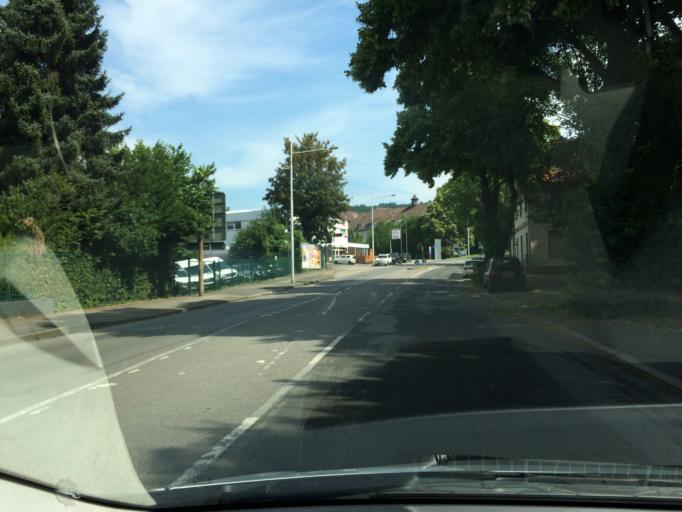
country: DE
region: North Rhine-Westphalia
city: Iserlohn
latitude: 51.3825
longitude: 7.7176
